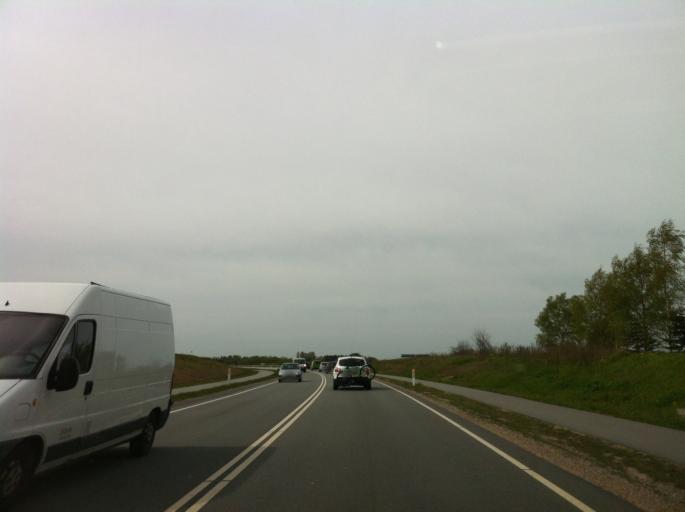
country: DK
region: Capital Region
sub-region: Frederikssund Kommune
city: Slangerup
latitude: 55.8941
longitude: 12.2110
